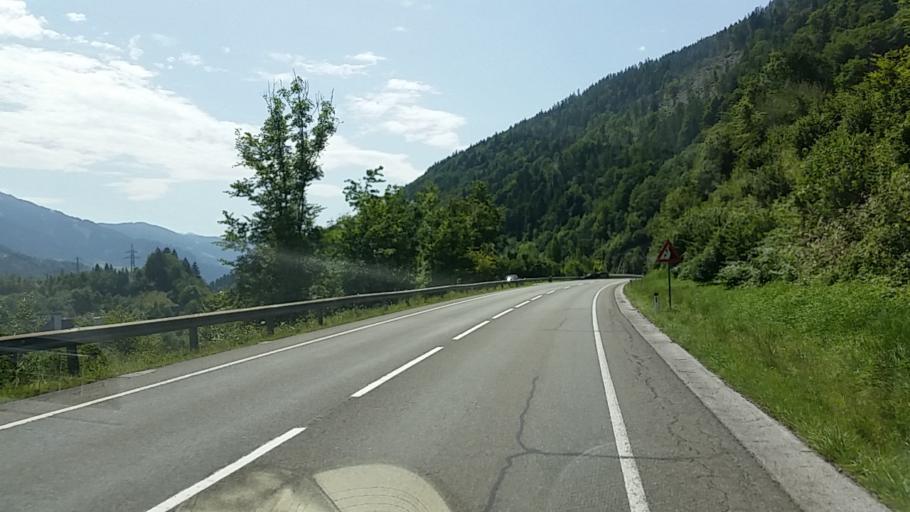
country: AT
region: Salzburg
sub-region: Politischer Bezirk Sankt Johann im Pongau
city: Pfarrwerfen
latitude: 47.4412
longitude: 13.2092
